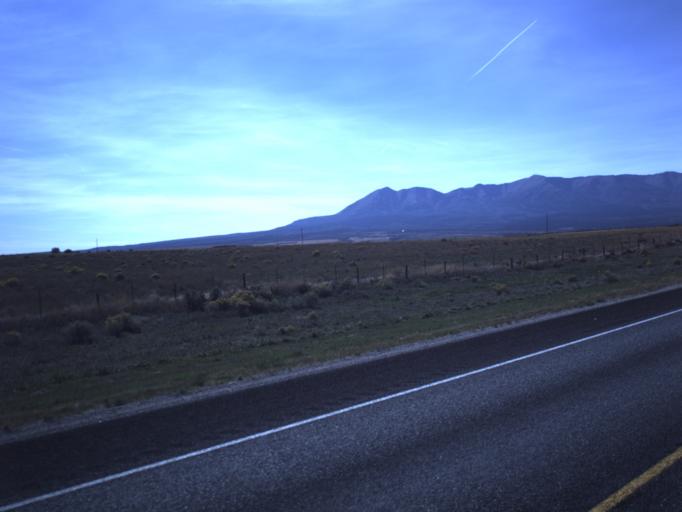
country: US
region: Utah
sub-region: San Juan County
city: Monticello
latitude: 37.8676
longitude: -109.2406
